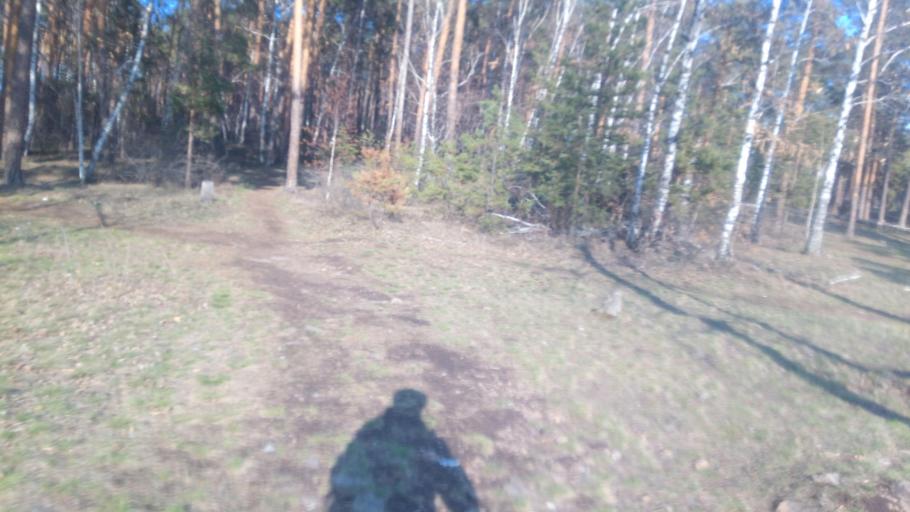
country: RU
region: Chelyabinsk
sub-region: Gorod Chelyabinsk
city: Chelyabinsk
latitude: 55.1597
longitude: 61.3231
